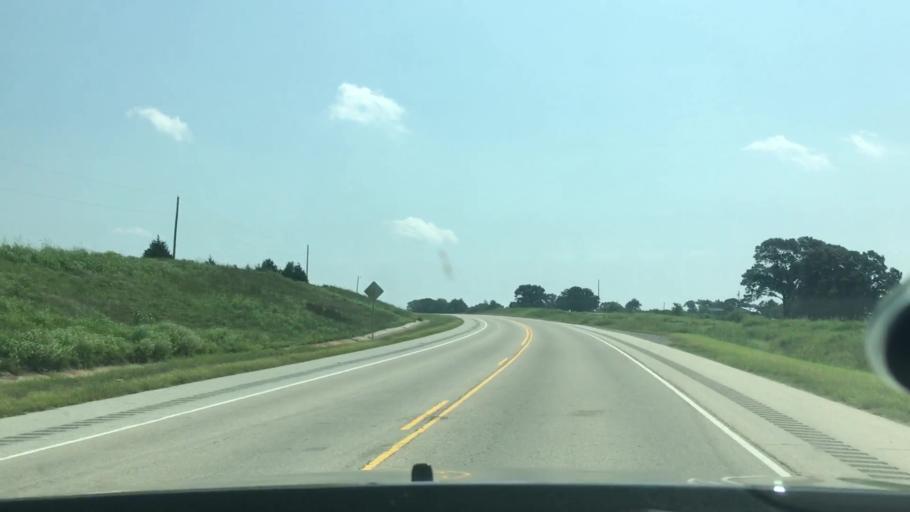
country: US
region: Oklahoma
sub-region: Atoka County
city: Atoka
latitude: 34.2903
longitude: -95.9710
